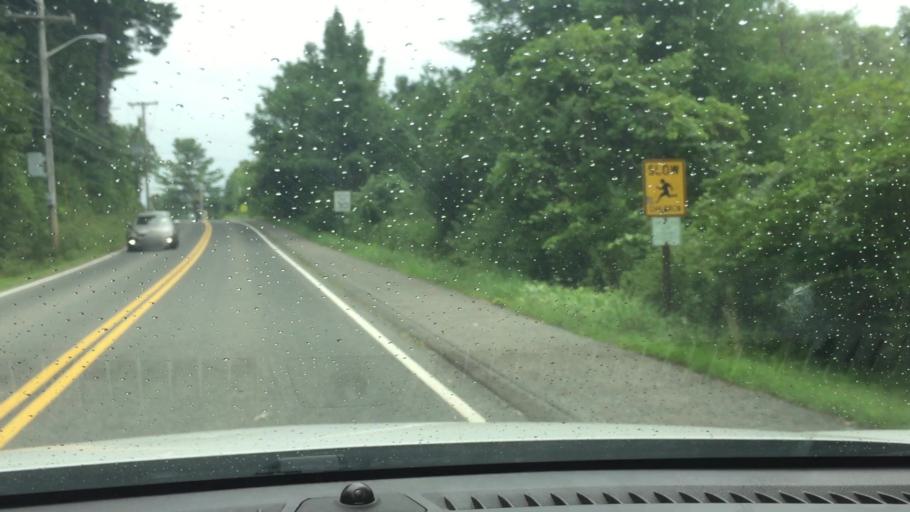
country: US
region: Massachusetts
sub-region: Berkshire County
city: Lenox
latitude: 42.3548
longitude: -73.2591
